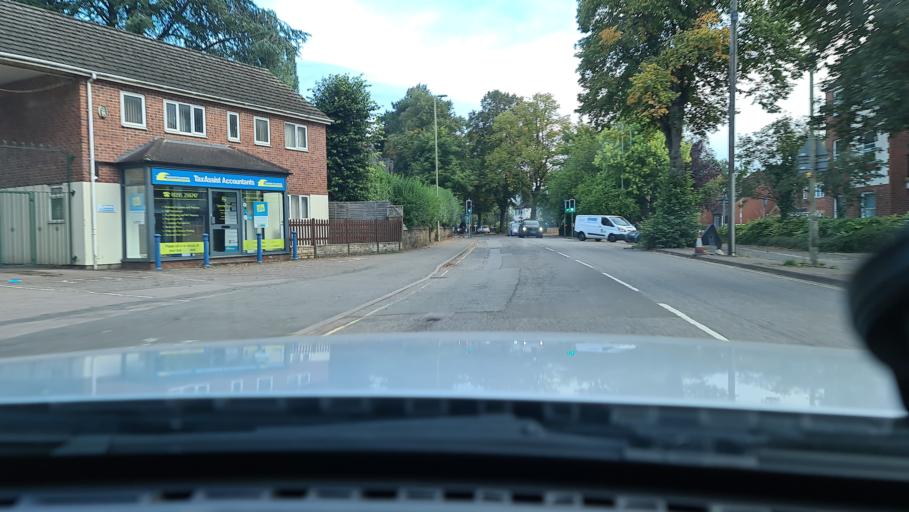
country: GB
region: England
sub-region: Oxfordshire
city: Banbury
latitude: 52.0652
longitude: -1.3398
